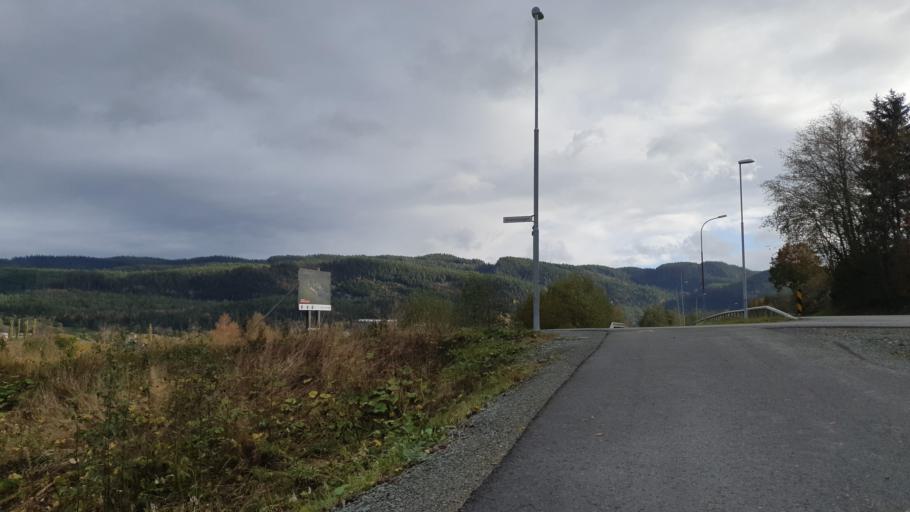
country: NO
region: Sor-Trondelag
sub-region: Klaebu
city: Klaebu
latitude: 63.3025
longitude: 10.4673
